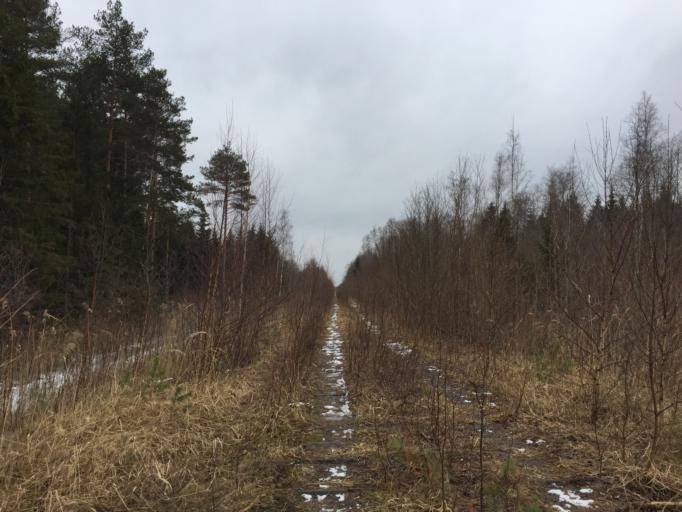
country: LV
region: Lielvarde
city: Lielvarde
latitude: 56.7622
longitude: 24.8188
